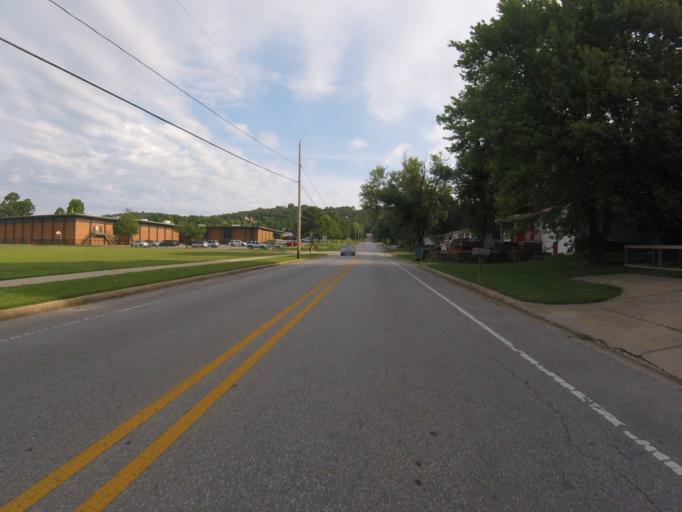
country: US
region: Arkansas
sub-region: Washington County
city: Fayetteville
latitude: 36.0573
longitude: -94.1893
